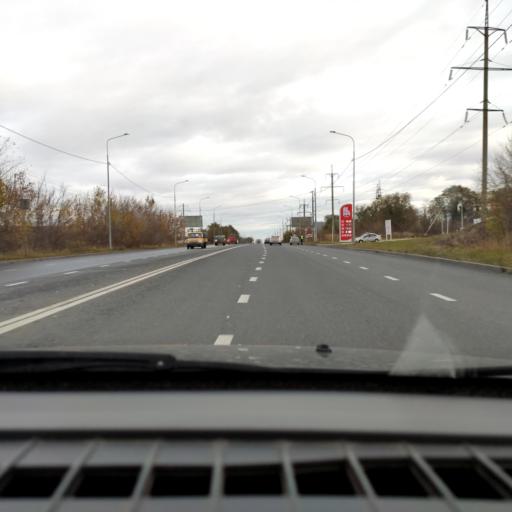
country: RU
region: Samara
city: Tol'yatti
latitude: 53.5676
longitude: 49.2912
